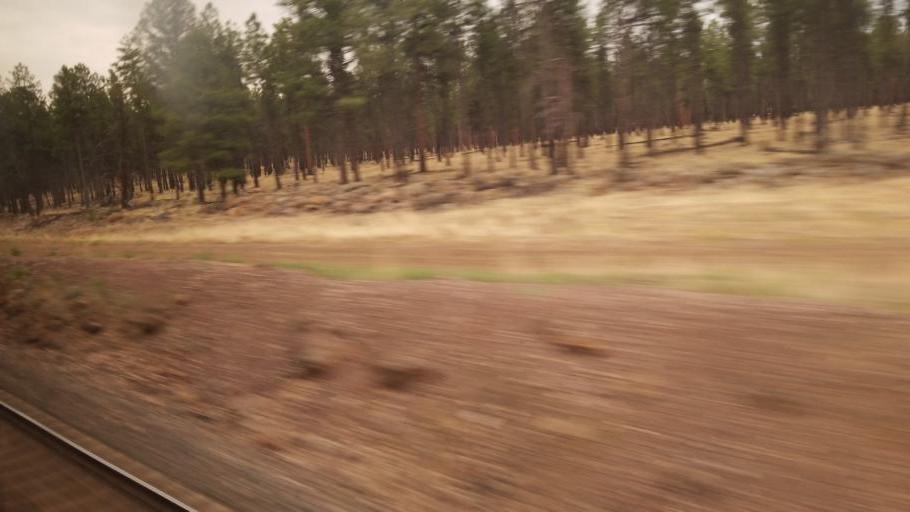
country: US
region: Arizona
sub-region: Coconino County
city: Parks
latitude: 35.2459
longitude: -112.0429
